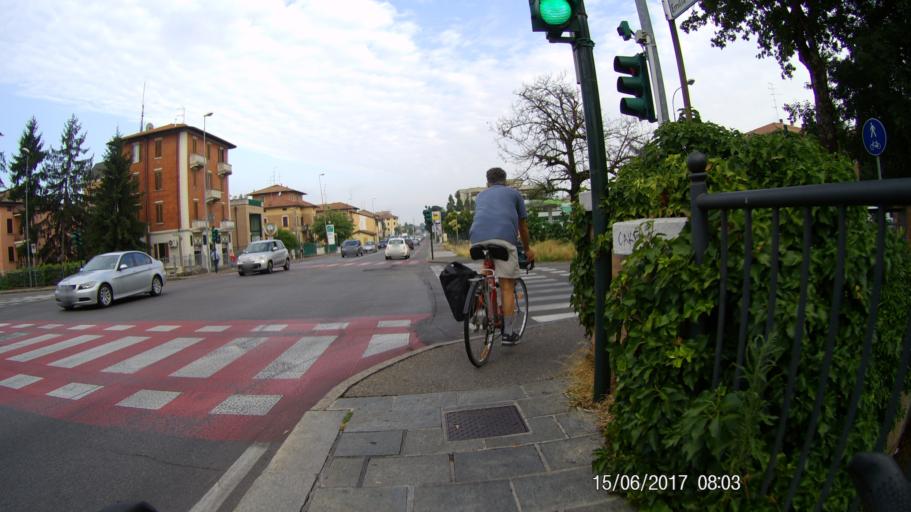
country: IT
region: Emilia-Romagna
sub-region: Provincia di Reggio Emilia
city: Reggio nell'Emilia
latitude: 44.7029
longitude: 10.6187
